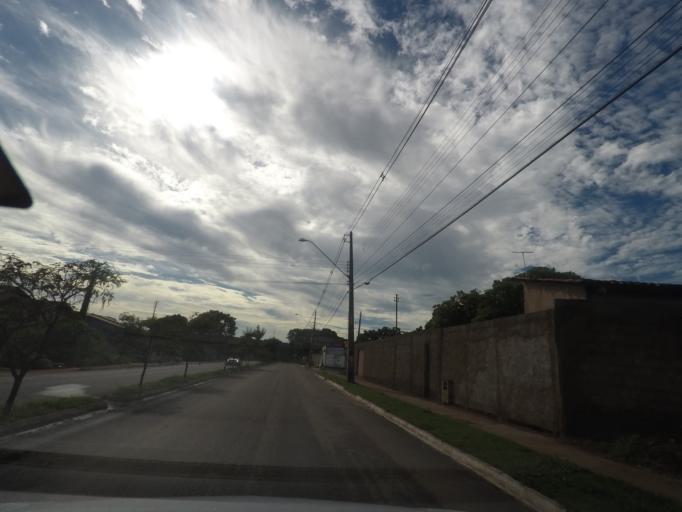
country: BR
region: Goias
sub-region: Aparecida De Goiania
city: Aparecida de Goiania
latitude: -16.8174
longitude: -49.3079
